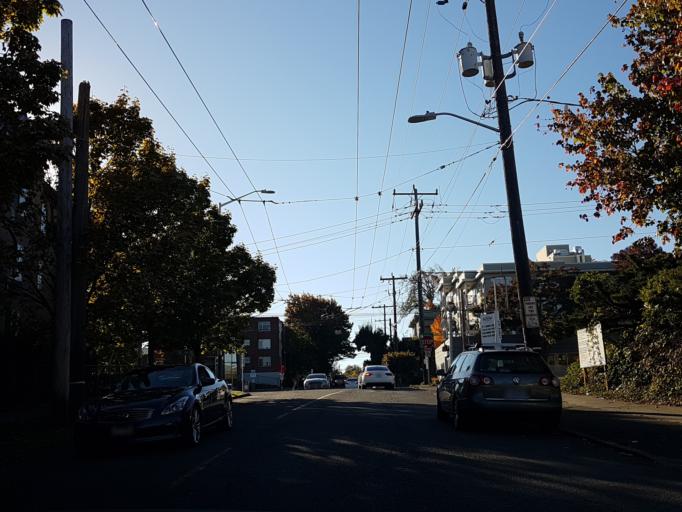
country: US
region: Washington
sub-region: King County
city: Seattle
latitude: 47.6263
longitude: -122.3468
